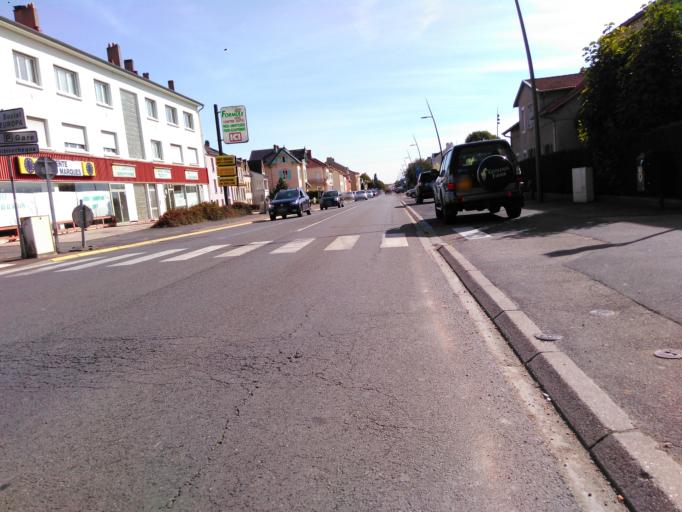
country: FR
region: Lorraine
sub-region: Departement de la Moselle
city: Hettange-Grande
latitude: 49.4043
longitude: 6.1570
